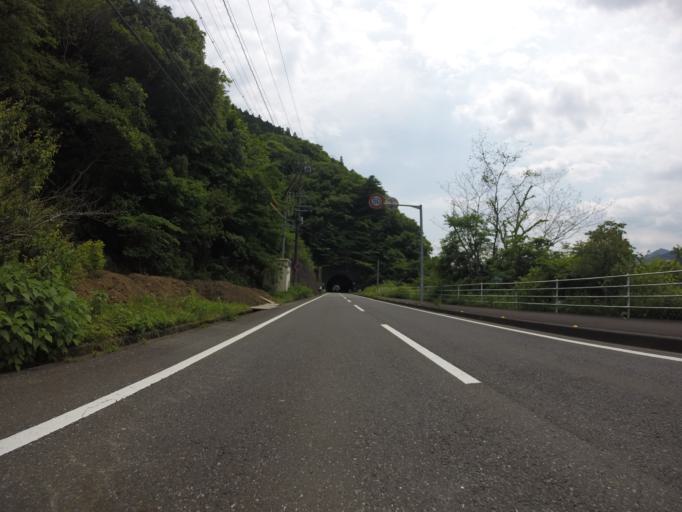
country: JP
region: Shizuoka
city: Shizuoka-shi
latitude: 35.0893
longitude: 138.3759
